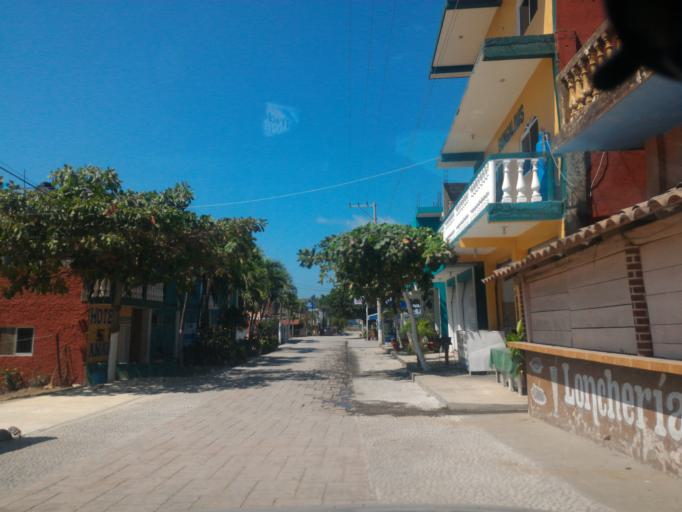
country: MX
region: Michoacan
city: Coahuayana Viejo
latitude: 18.5804
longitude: -103.6696
